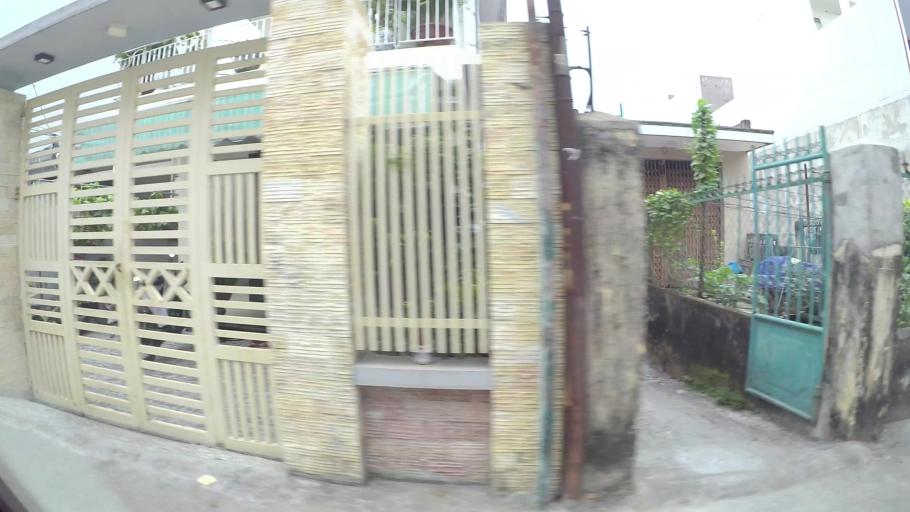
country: VN
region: Da Nang
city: Da Nang
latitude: 16.0449
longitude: 108.2074
